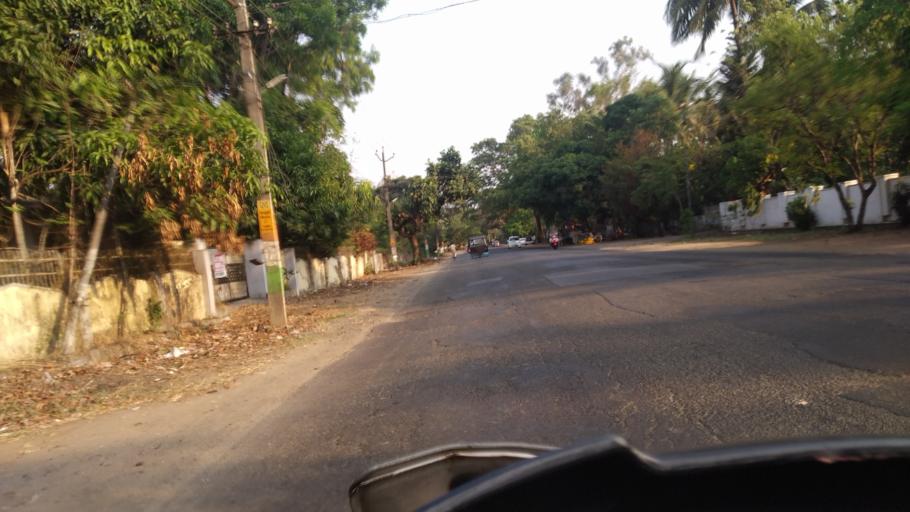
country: IN
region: Kerala
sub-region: Thrissur District
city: Thanniyam
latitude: 10.4334
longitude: 76.0985
